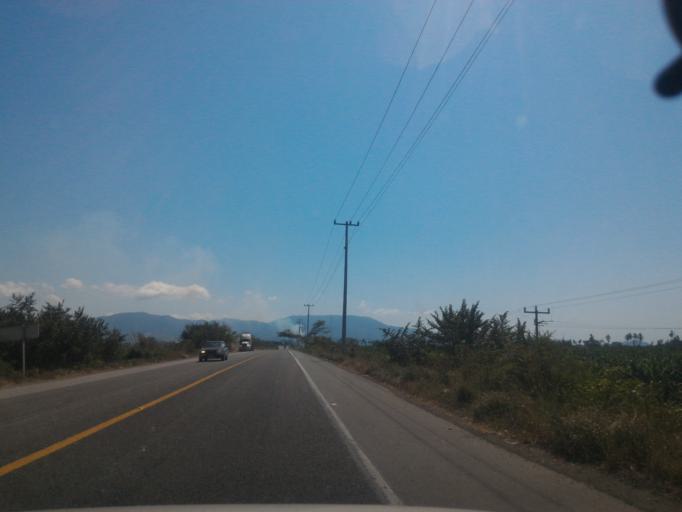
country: MX
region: Michoacan
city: Coahuayana Viejo
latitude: 18.7237
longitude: -103.7217
